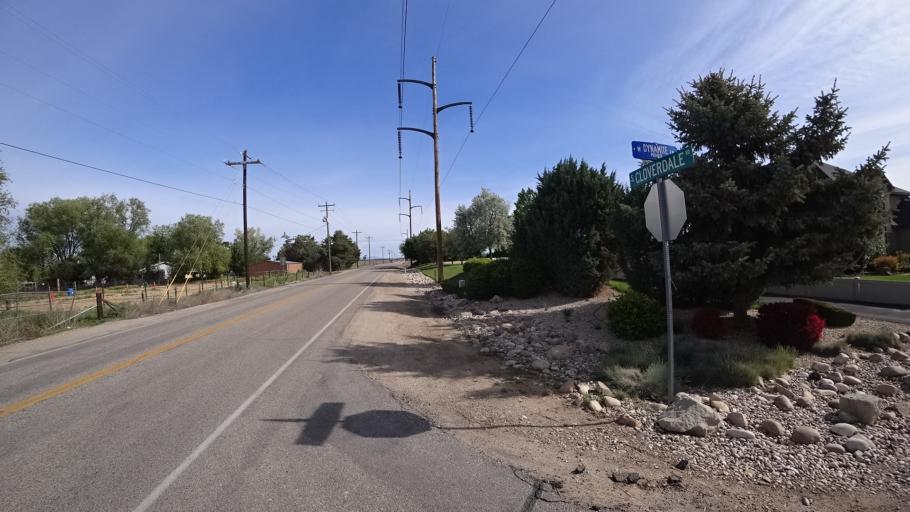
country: US
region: Idaho
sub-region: Ada County
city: Kuna
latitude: 43.4581
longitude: -116.3344
